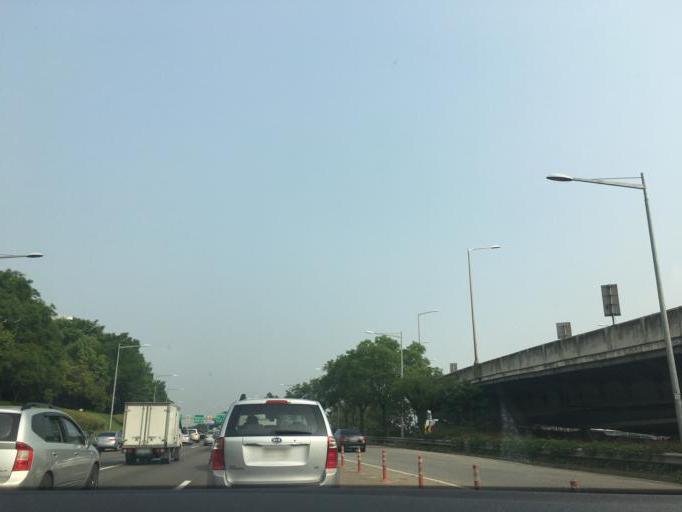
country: KR
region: Seoul
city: Seoul
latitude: 37.5207
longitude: 127.0636
